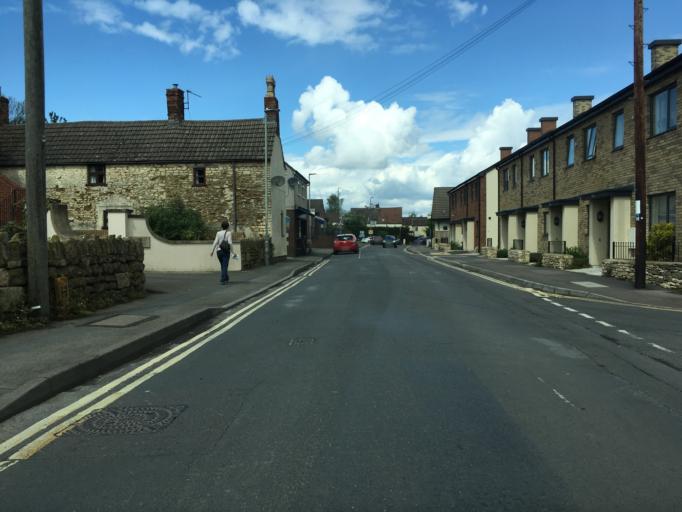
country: GB
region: England
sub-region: Gloucestershire
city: Dursley
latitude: 51.7005
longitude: -2.3632
